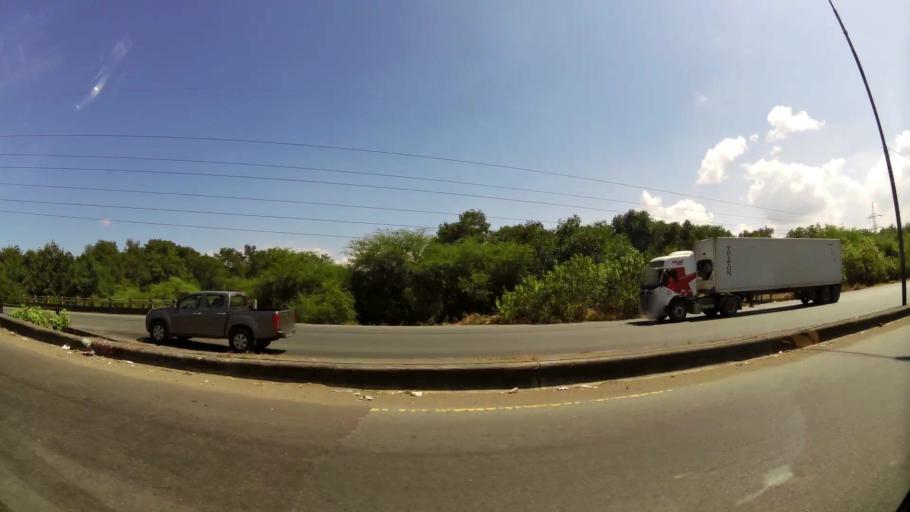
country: EC
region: Guayas
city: Santa Lucia
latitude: -2.1958
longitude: -79.9585
